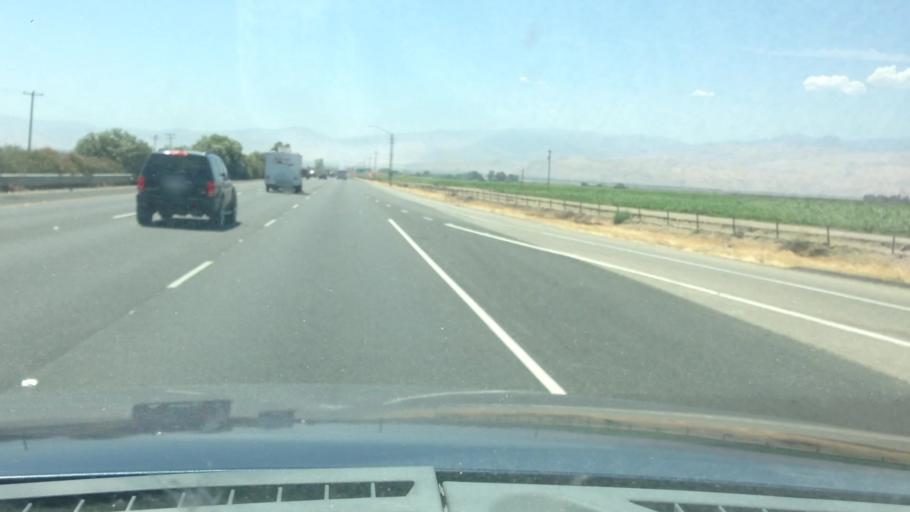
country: US
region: California
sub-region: Kern County
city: Greenfield
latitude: 35.1674
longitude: -119.0028
